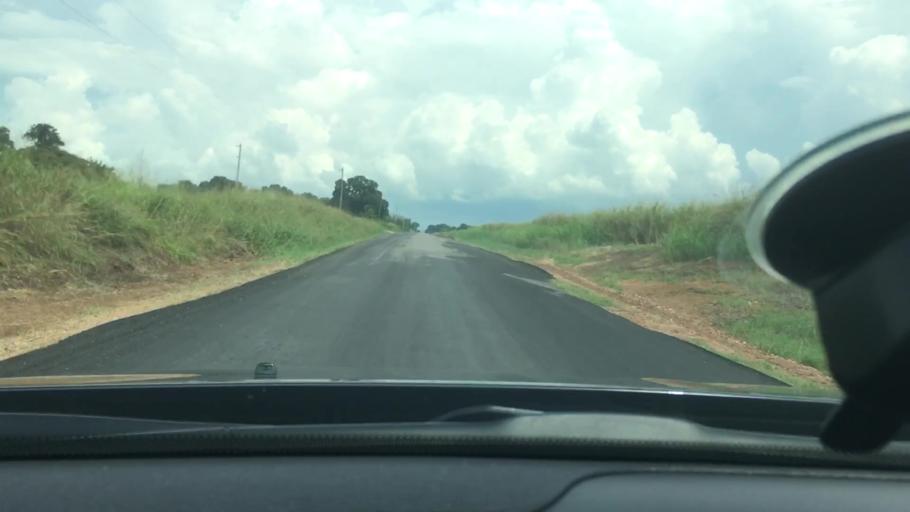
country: US
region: Oklahoma
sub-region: Carter County
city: Dickson
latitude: 34.2042
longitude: -96.8982
